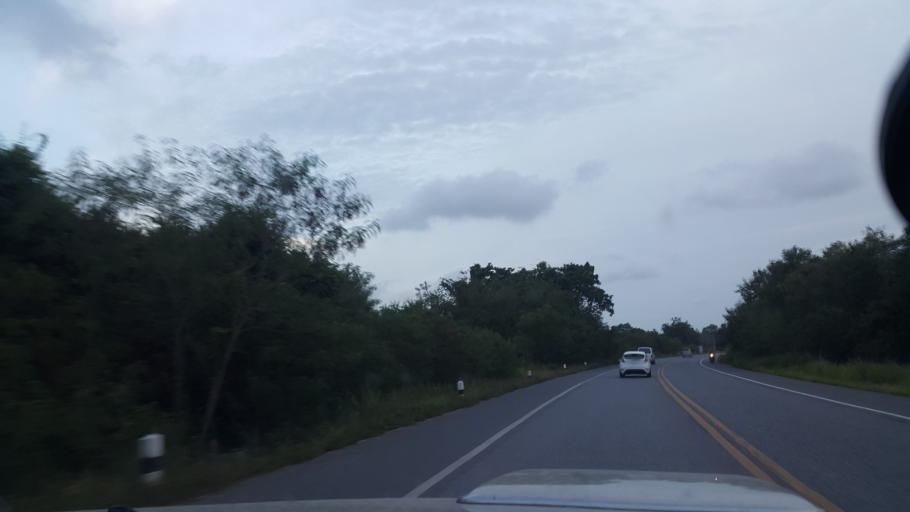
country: TH
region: Rayong
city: Ban Chang
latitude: 12.7097
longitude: 101.0070
